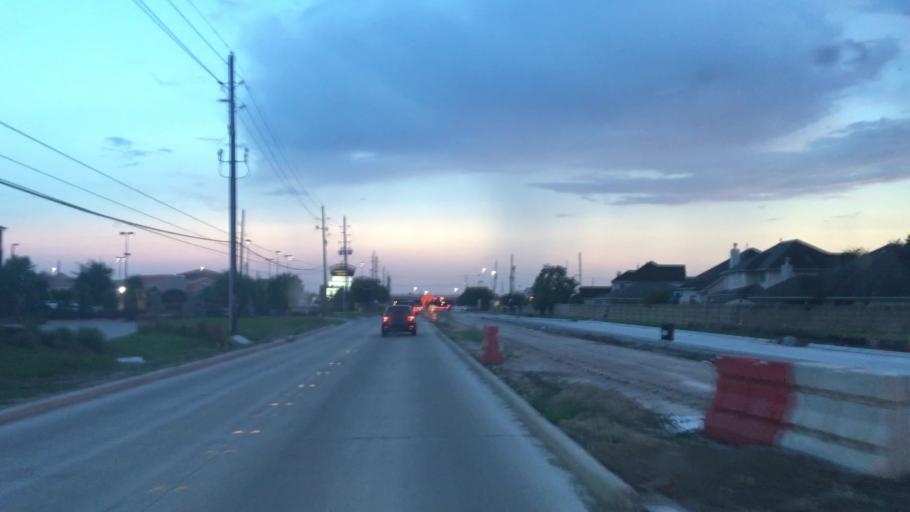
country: US
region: Texas
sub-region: Harris County
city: Humble
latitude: 29.9393
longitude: -95.2496
